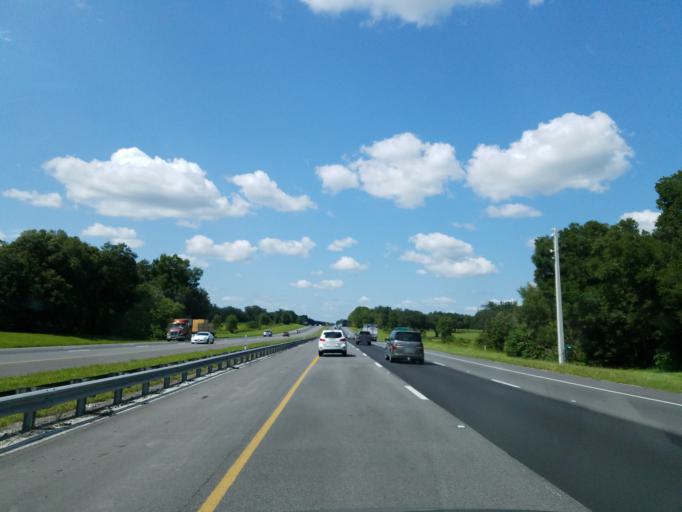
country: US
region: Florida
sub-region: Marion County
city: Ocala
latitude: 29.2805
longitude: -82.1979
